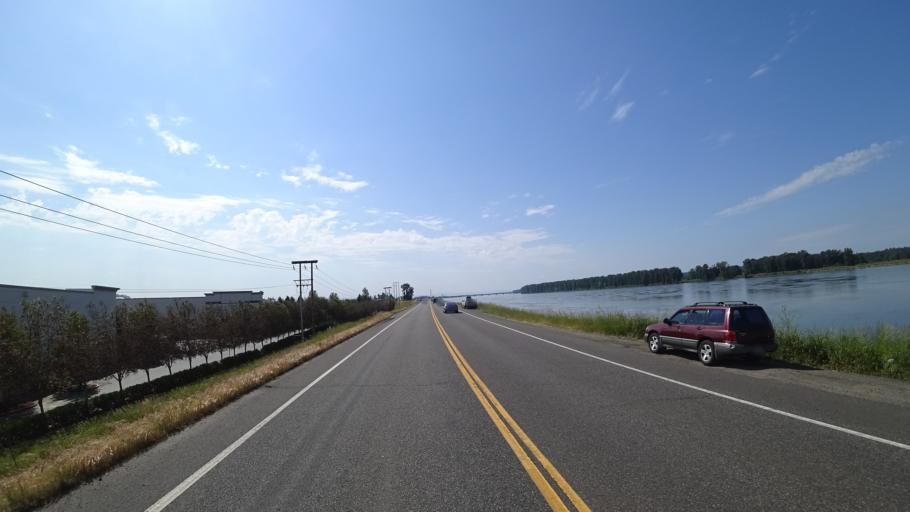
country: US
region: Washington
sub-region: Clark County
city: Mill Plain
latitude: 45.5634
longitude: -122.5118
